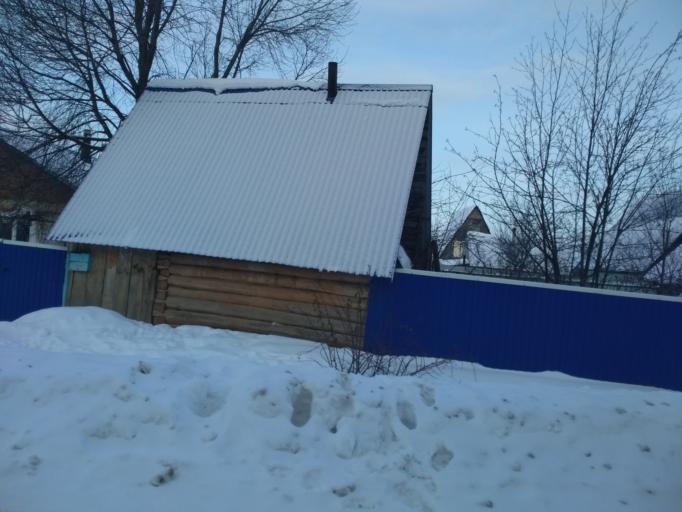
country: RU
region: Bashkortostan
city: Iglino
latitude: 54.7696
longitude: 56.5321
